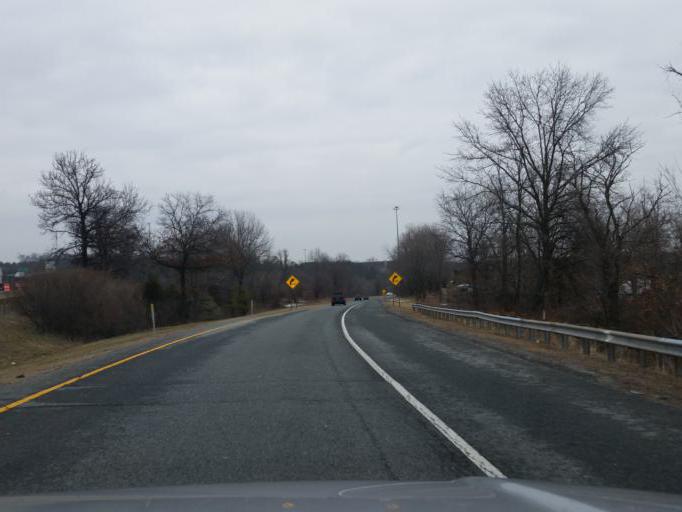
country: US
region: Maryland
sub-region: Baltimore County
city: Arbutus
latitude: 39.2476
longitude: -76.6832
